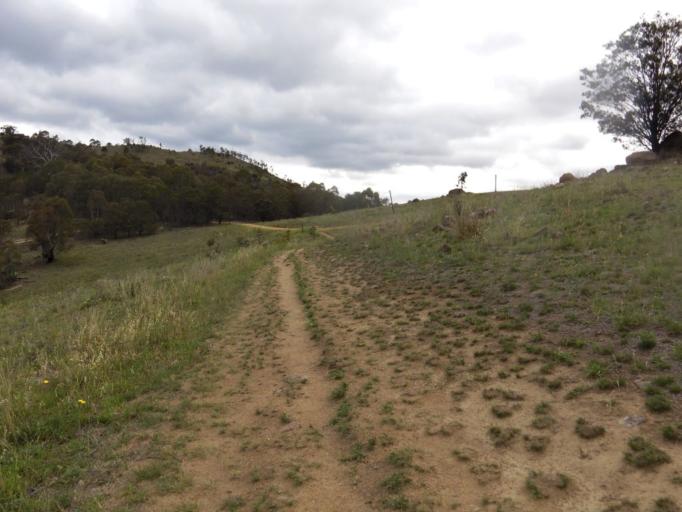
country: AU
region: Australian Capital Territory
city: Macarthur
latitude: -35.3657
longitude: 149.0413
